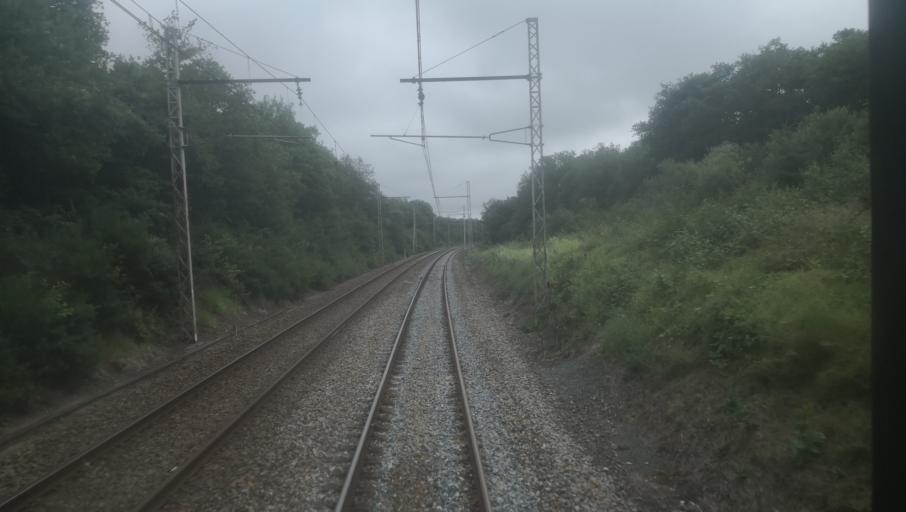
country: FR
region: Centre
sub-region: Departement de l'Indre
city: Saint-Maur
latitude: 46.7637
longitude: 1.6062
